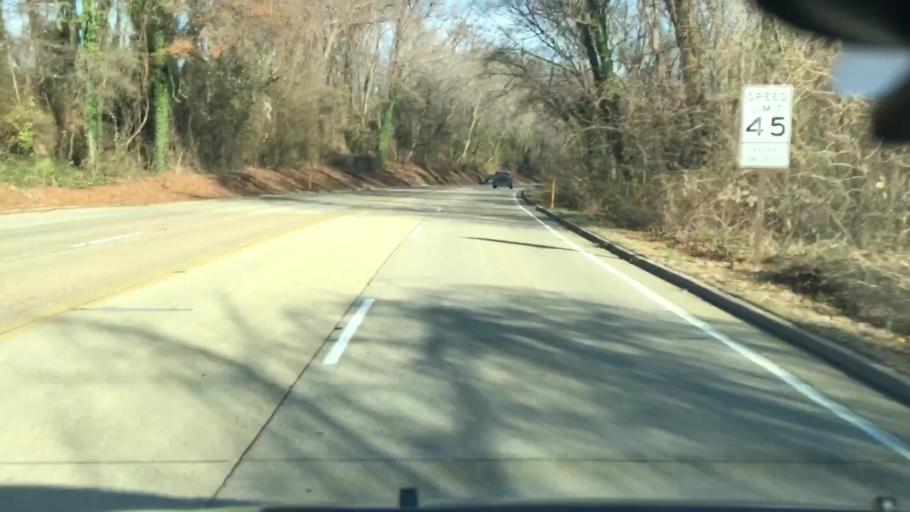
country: US
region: Virginia
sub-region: Fairfax County
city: Fort Hunt
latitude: 38.7523
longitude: -77.0500
